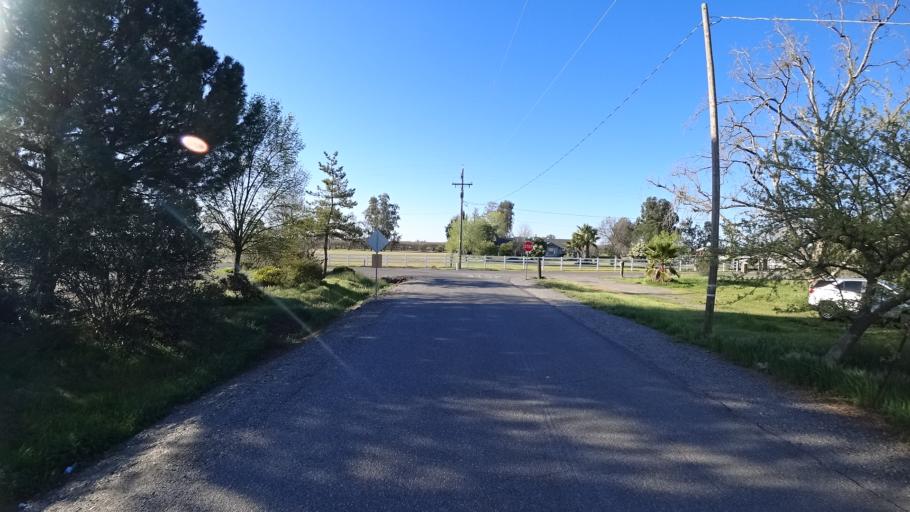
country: US
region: California
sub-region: Glenn County
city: Orland
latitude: 39.7552
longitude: -122.2272
